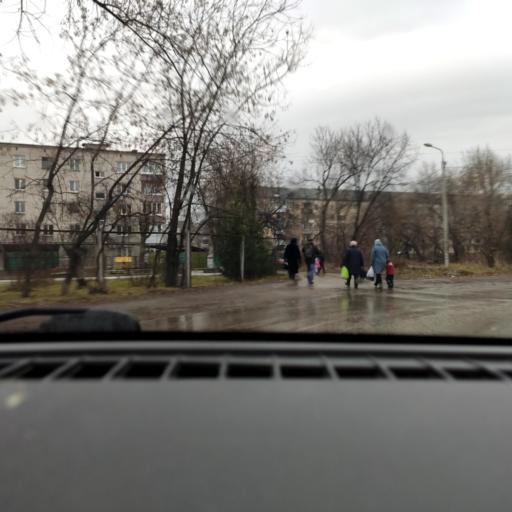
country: RU
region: Perm
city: Kultayevo
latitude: 57.9984
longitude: 55.9359
